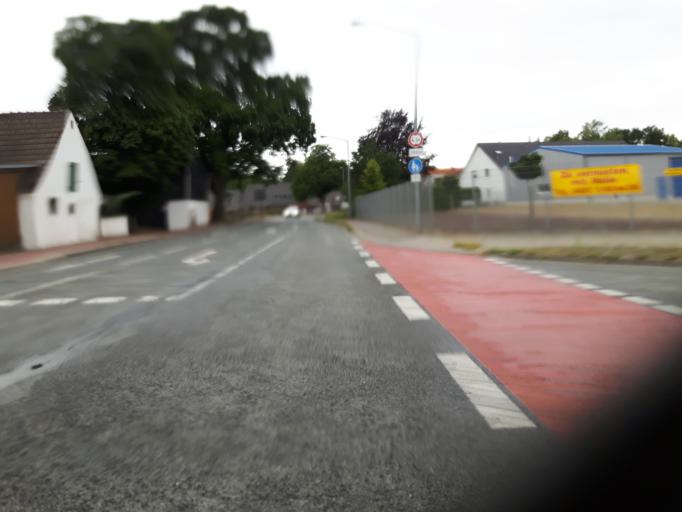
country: DE
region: Lower Saxony
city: Stuhr
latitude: 53.0162
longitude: 8.7734
